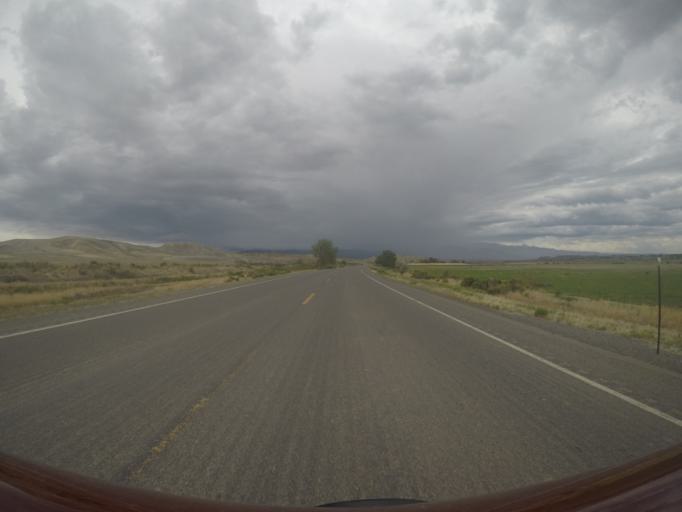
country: US
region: Wyoming
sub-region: Big Horn County
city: Lovell
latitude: 44.8767
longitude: -108.3048
